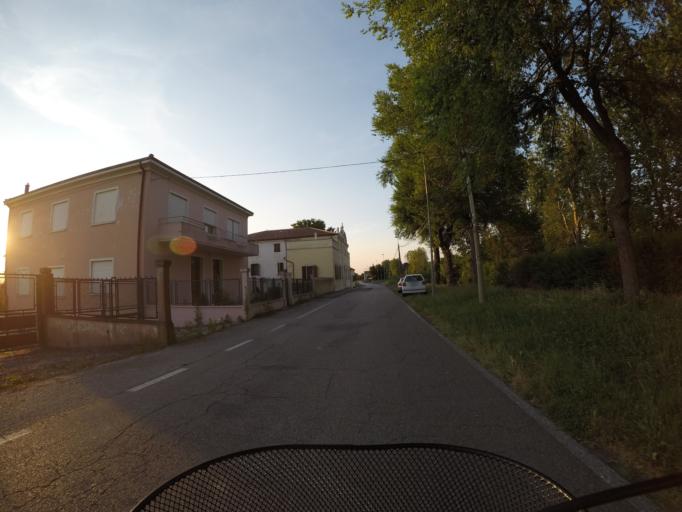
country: IT
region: Veneto
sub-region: Provincia di Rovigo
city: Fratta Polesine
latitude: 45.0343
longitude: 11.6410
